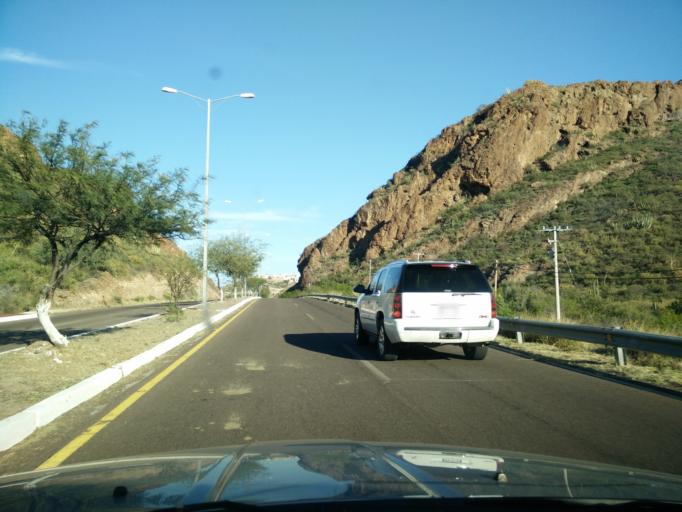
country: MX
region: Sonora
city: Heroica Guaymas
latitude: 27.9504
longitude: -111.0725
